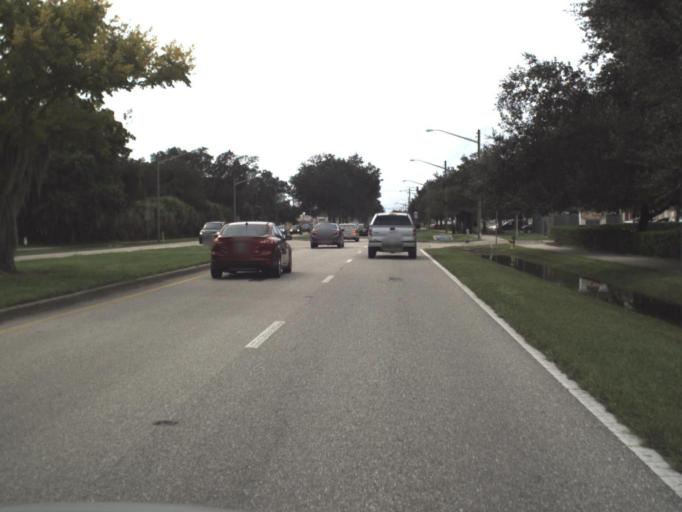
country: US
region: Florida
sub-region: Sarasota County
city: Nokomis
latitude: 27.0998
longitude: -82.4268
